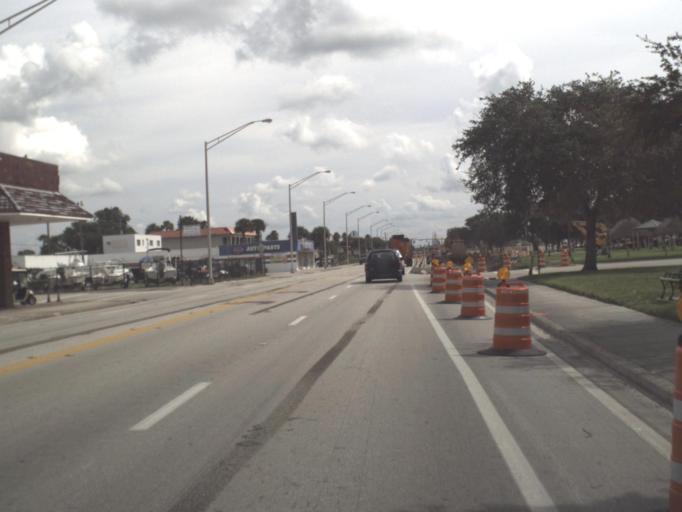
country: US
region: Florida
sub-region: Okeechobee County
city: Okeechobee
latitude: 27.2437
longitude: -80.8340
